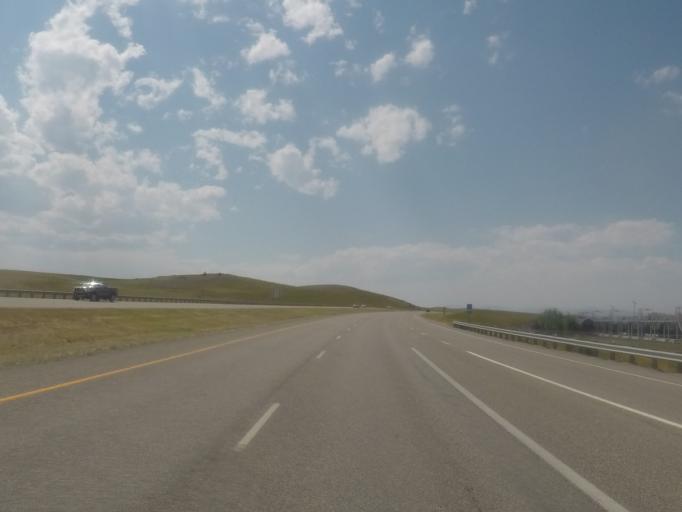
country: US
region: Montana
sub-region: Gallatin County
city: Three Forks
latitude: 45.8821
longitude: -111.4425
